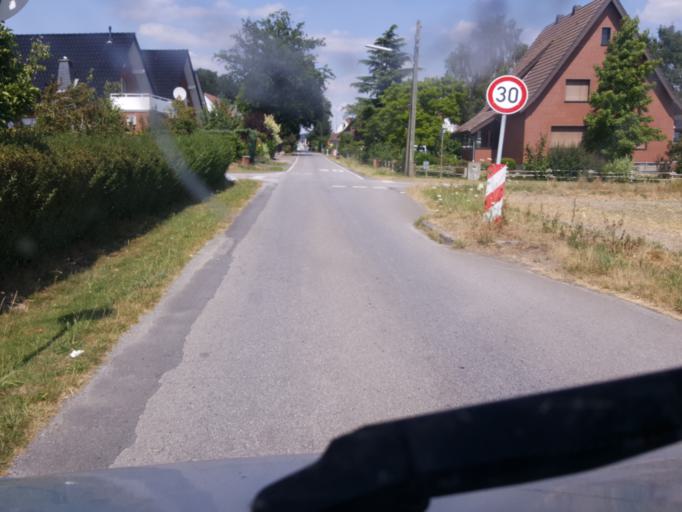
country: DE
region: North Rhine-Westphalia
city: Bad Oeynhausen
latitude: 52.2255
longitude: 8.7631
